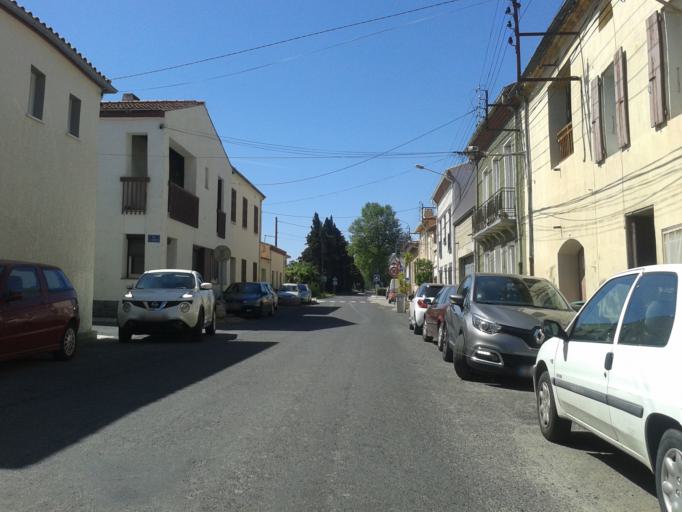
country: FR
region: Languedoc-Roussillon
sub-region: Departement des Pyrenees-Orientales
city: Corneilla-la-Riviere
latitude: 42.6987
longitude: 2.7282
